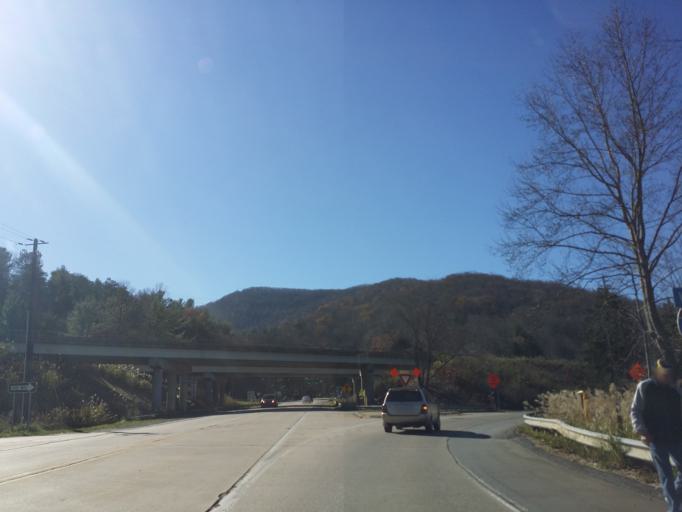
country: US
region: North Carolina
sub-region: Buncombe County
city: Swannanoa
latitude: 35.5819
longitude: -82.4634
